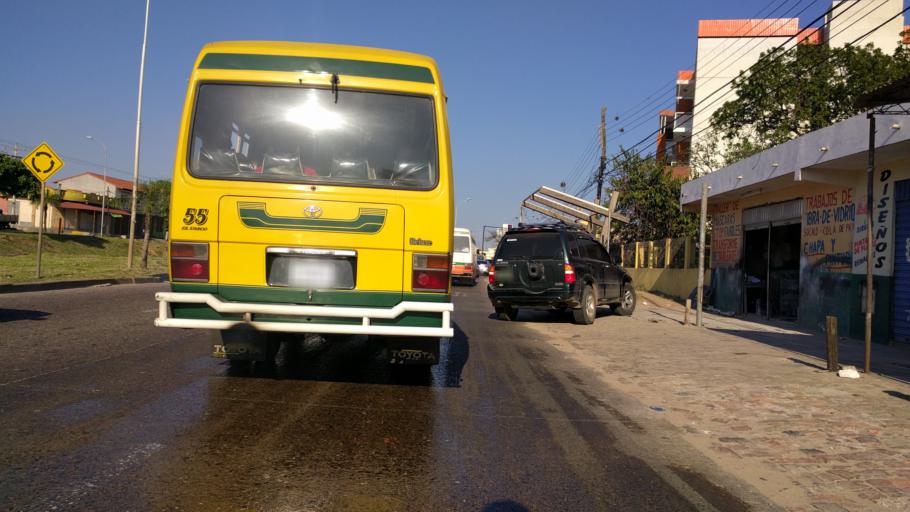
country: BO
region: Santa Cruz
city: Santa Cruz de la Sierra
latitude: -17.8215
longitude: -63.1757
